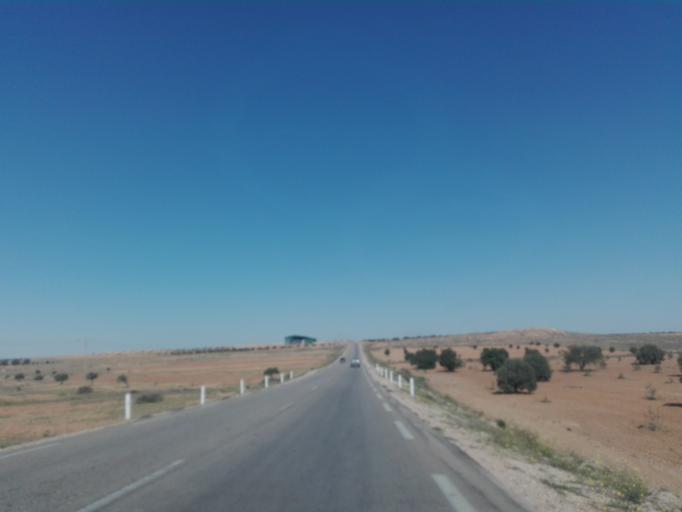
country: TN
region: Safaqis
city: Bi'r `Ali Bin Khalifah
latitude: 34.7324
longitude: 10.4218
